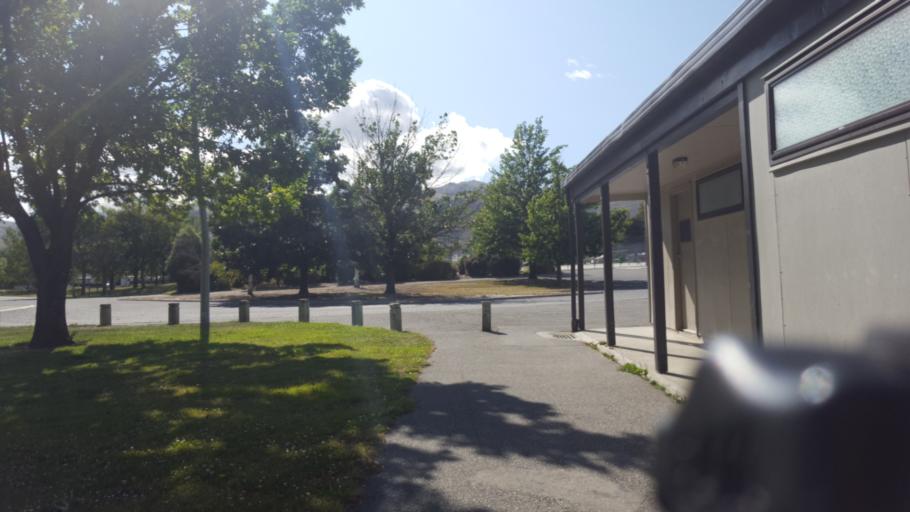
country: NZ
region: Otago
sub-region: Queenstown-Lakes District
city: Wanaka
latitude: -45.0421
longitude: 169.1946
